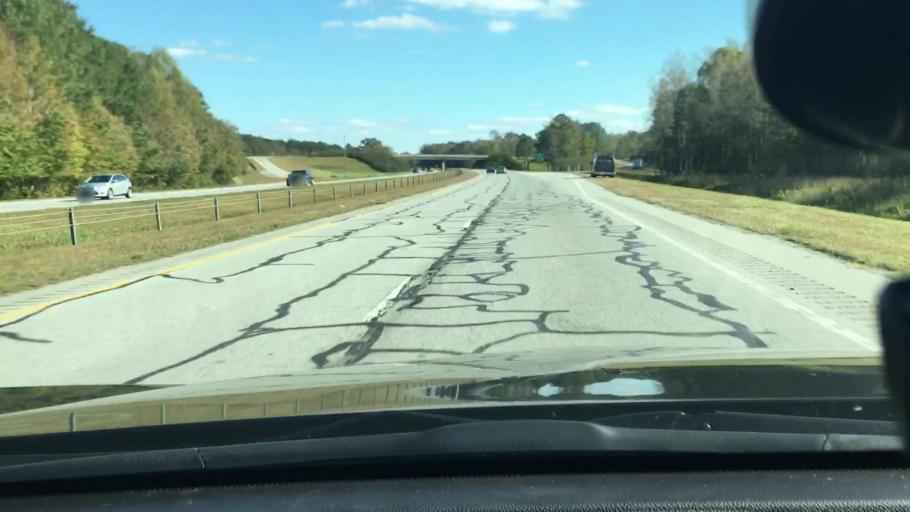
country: US
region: North Carolina
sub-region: Pitt County
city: Farmville
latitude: 35.6009
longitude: -77.5621
